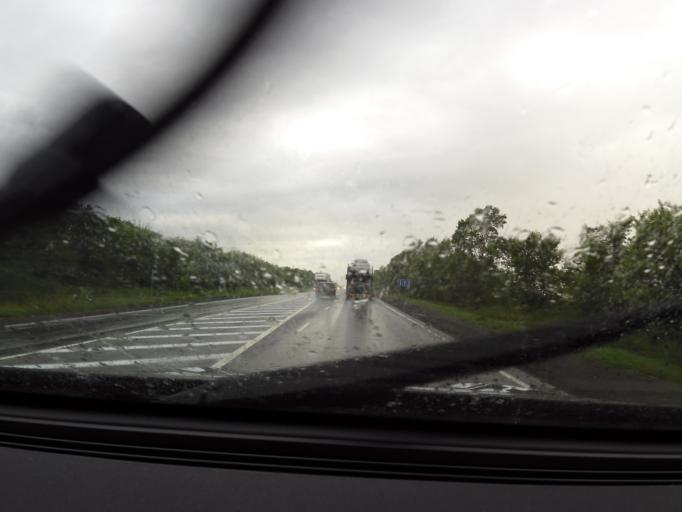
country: RU
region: Chuvashia
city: Yantikovo
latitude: 55.8017
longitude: 47.8829
